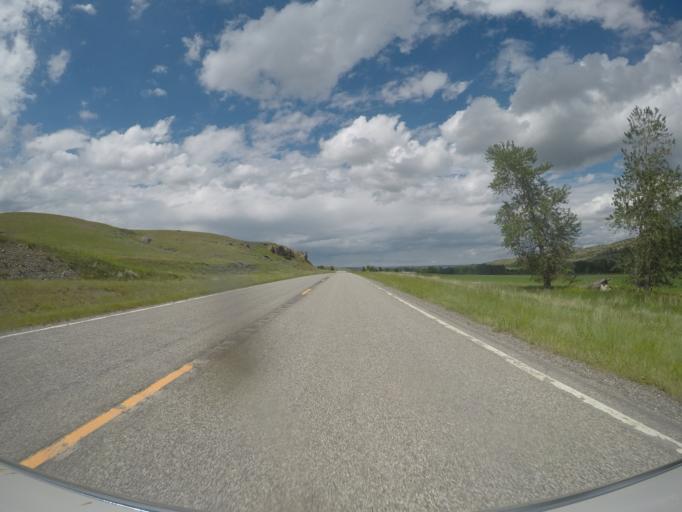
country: US
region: Montana
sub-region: Sweet Grass County
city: Big Timber
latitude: 45.7459
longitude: -109.9951
